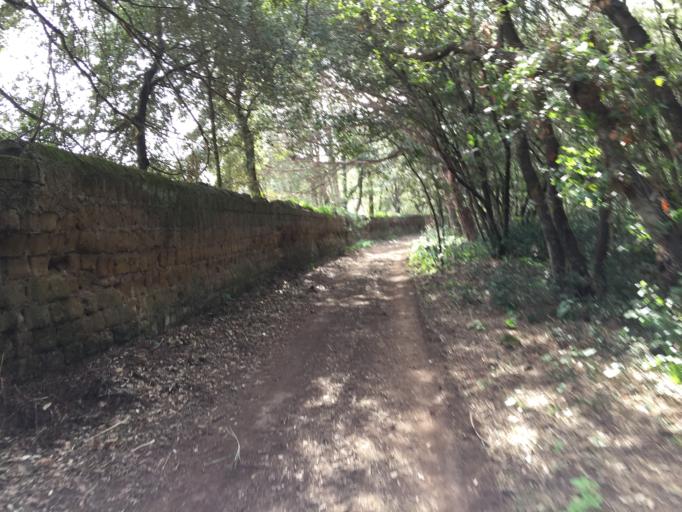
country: IT
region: Campania
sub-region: Provincia di Napoli
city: Monterusciello
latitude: 40.8475
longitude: 14.0506
